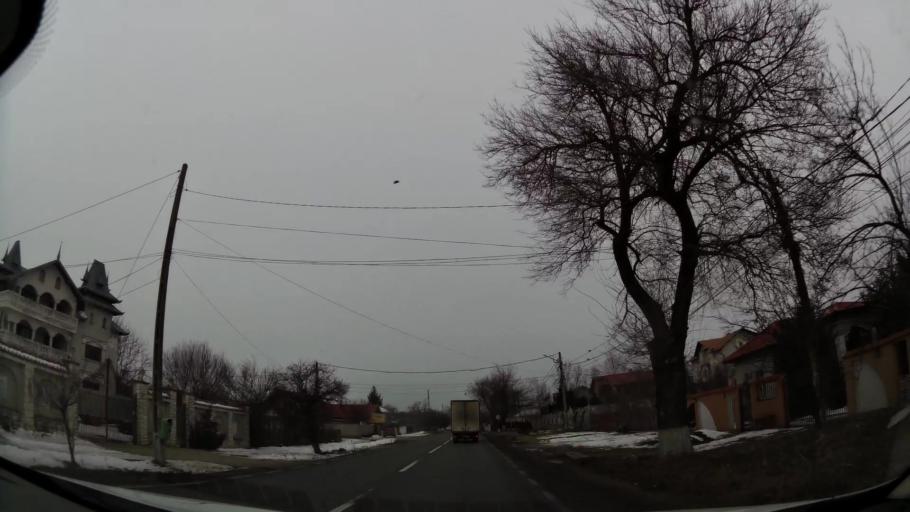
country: RO
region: Dambovita
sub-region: Comuna Tartasesti
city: Baldana
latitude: 44.5920
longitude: 25.7900
